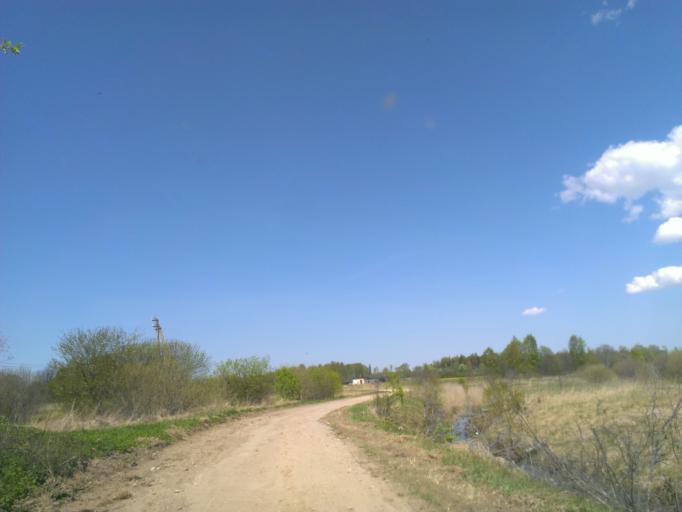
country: LV
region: Saulkrastu
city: Saulkrasti
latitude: 57.3341
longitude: 24.4873
